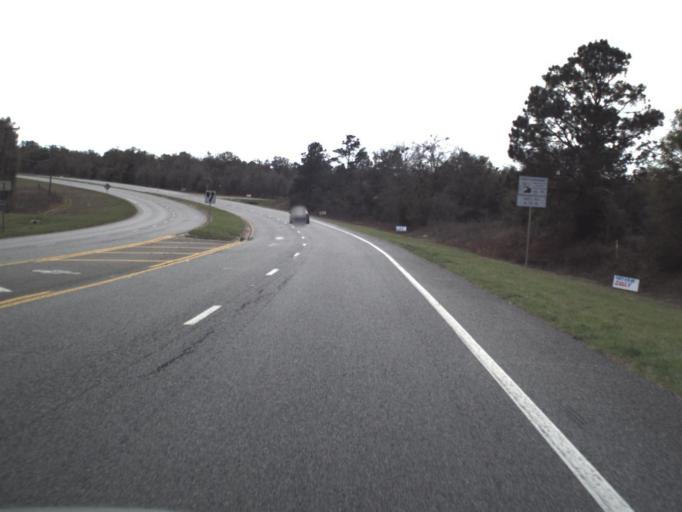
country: US
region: Florida
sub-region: Washington County
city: Chipley
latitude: 30.6463
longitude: -85.3994
